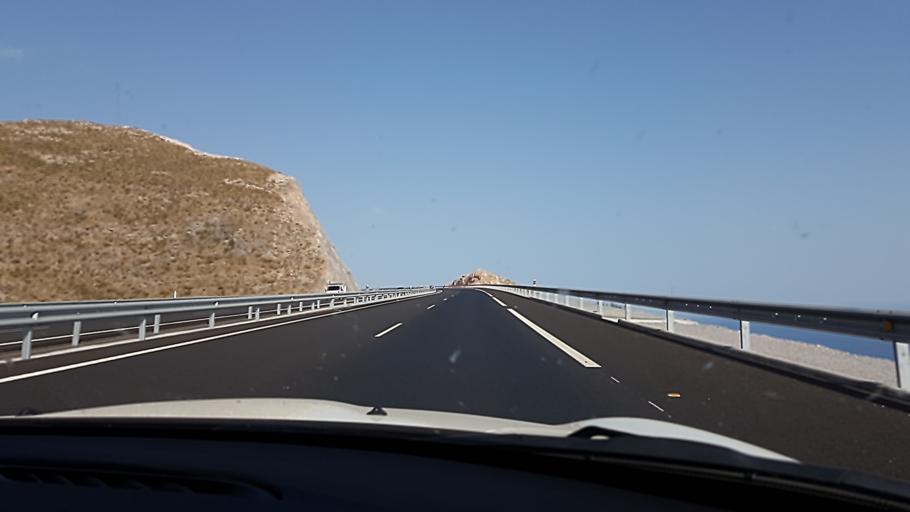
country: ES
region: Andalusia
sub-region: Provincia de Granada
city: Gualchos
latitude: 36.7154
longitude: -3.3911
